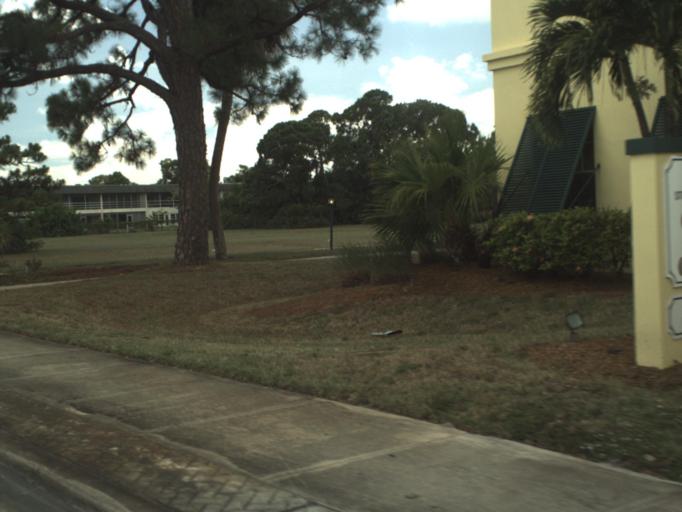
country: US
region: Florida
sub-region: Martin County
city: Stuart
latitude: 27.1832
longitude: -80.2532
